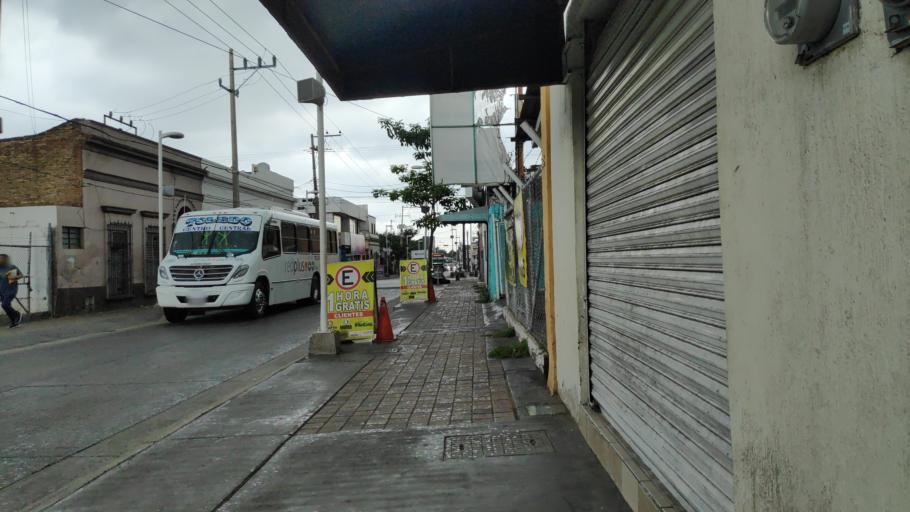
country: MX
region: Sinaloa
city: Culiacan
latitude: 24.8063
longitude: -107.3995
